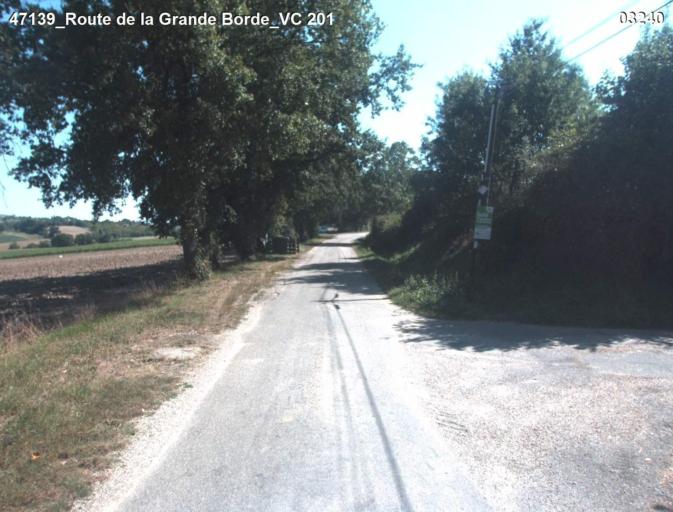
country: FR
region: Aquitaine
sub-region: Departement du Lot-et-Garonne
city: Nerac
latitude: 44.0882
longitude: 0.3795
